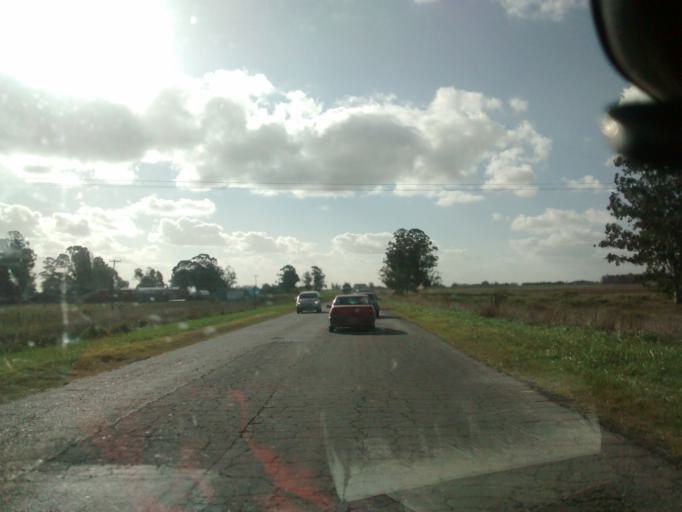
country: AR
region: Buenos Aires
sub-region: Partido de Ayacucho
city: Ayacucho
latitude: -37.1764
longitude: -58.5187
